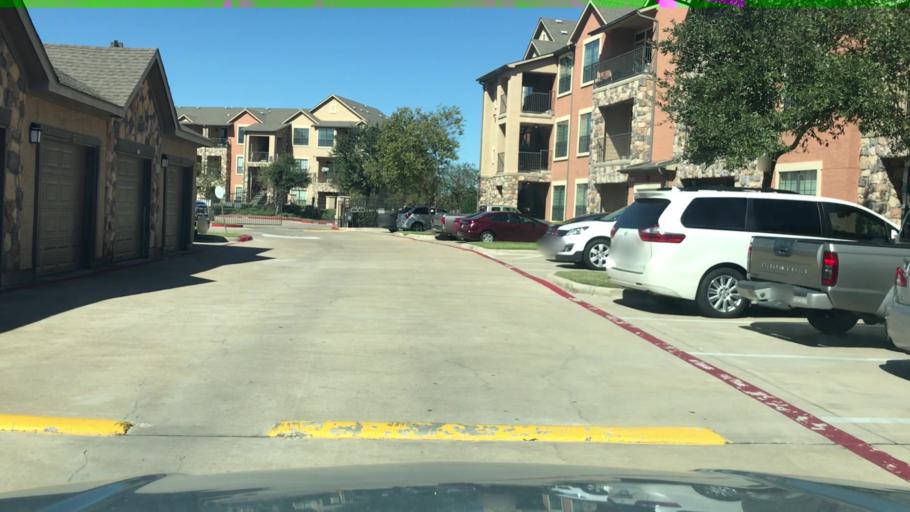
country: US
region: Texas
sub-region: Fort Bend County
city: Cinco Ranch
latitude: 29.7818
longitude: -95.7461
